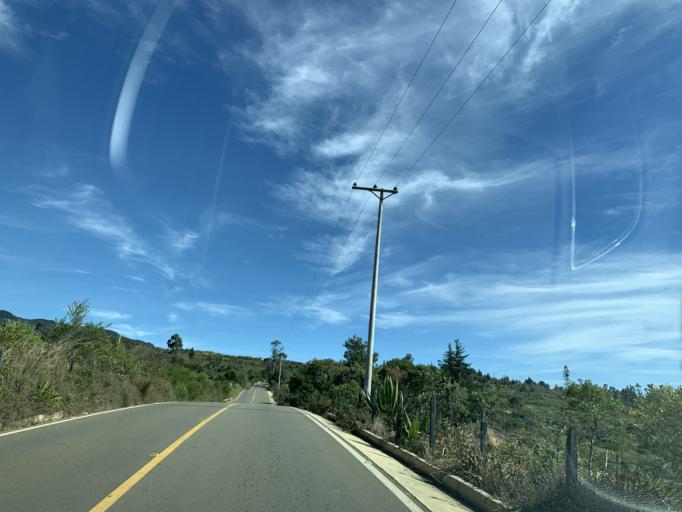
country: CO
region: Boyaca
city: Santa Sofia
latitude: 5.6965
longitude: -73.5900
